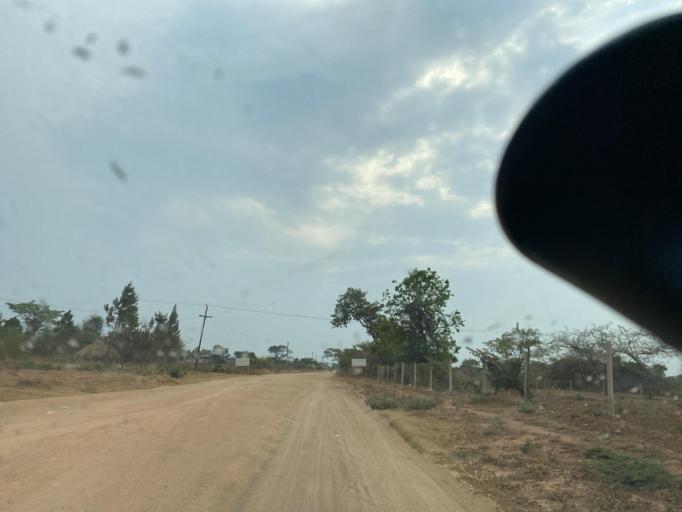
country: ZM
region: Lusaka
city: Lusaka
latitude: -15.2879
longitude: 28.2887
